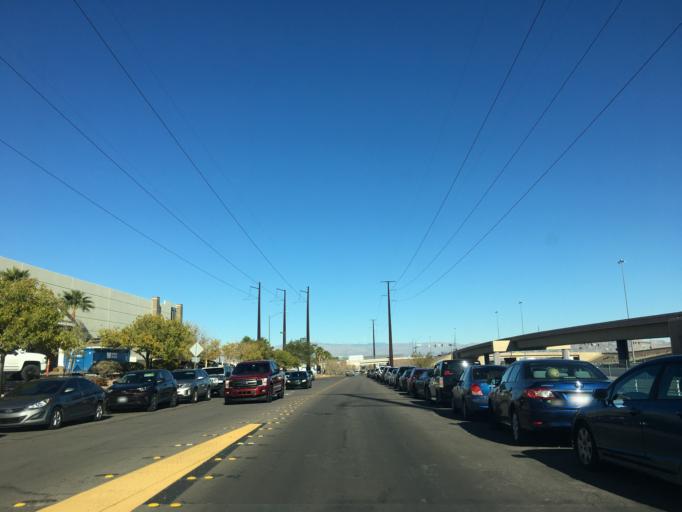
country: US
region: Nevada
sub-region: Clark County
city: Henderson
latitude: 36.0430
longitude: -115.0226
